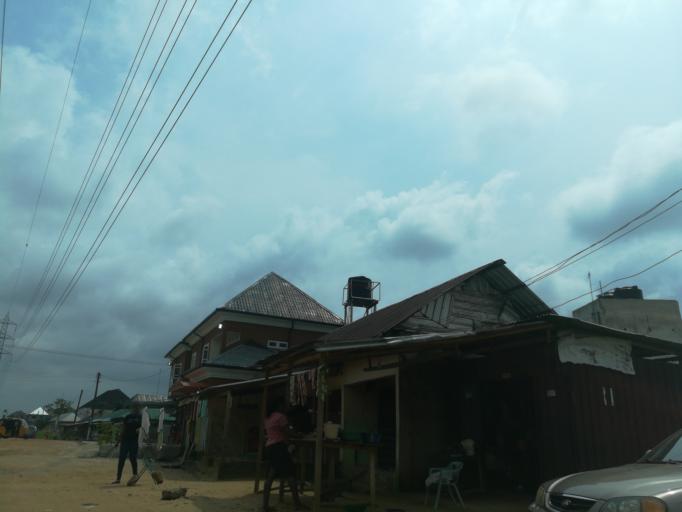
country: NG
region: Rivers
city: Port Harcourt
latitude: 4.8923
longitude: 6.9825
